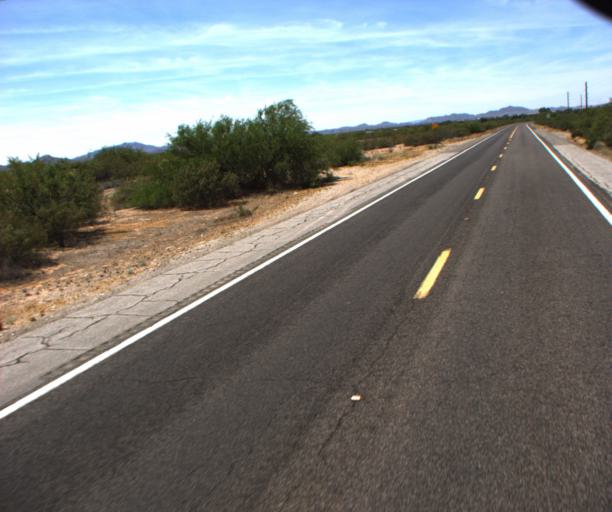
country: US
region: Arizona
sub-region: La Paz County
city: Salome
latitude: 33.8249
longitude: -113.5239
